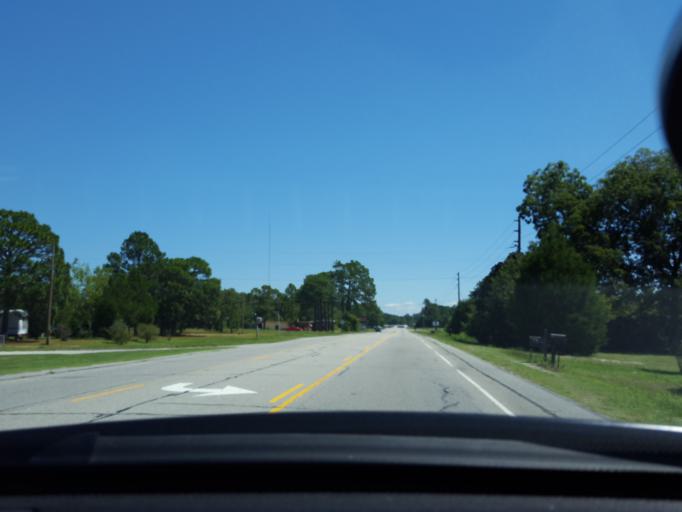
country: US
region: North Carolina
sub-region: Bladen County
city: Elizabethtown
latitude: 34.6478
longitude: -78.5771
